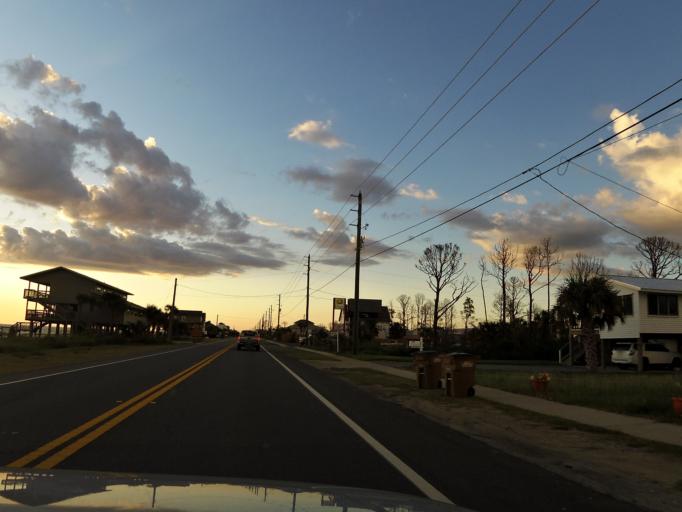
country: US
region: Florida
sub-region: Bay County
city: Mexico Beach
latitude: 29.8989
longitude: -85.3631
